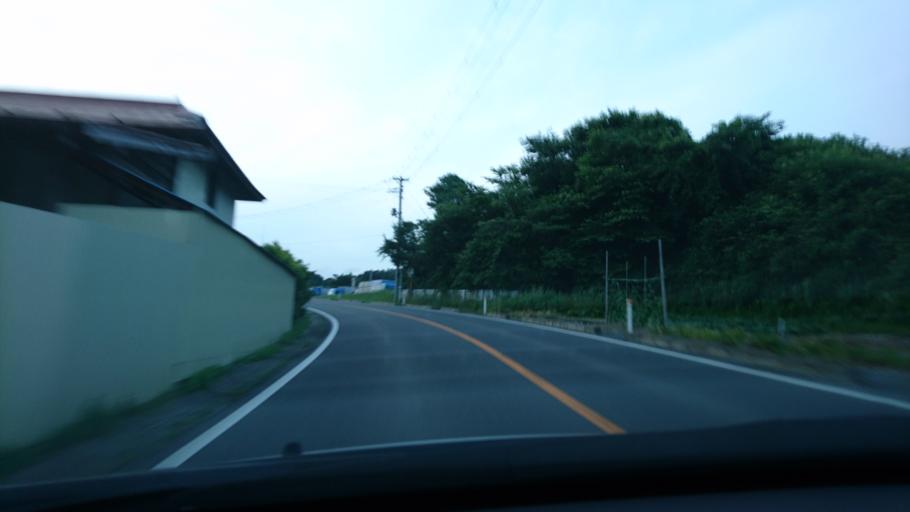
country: JP
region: Iwate
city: Ichinoseki
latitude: 38.7723
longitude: 140.9996
